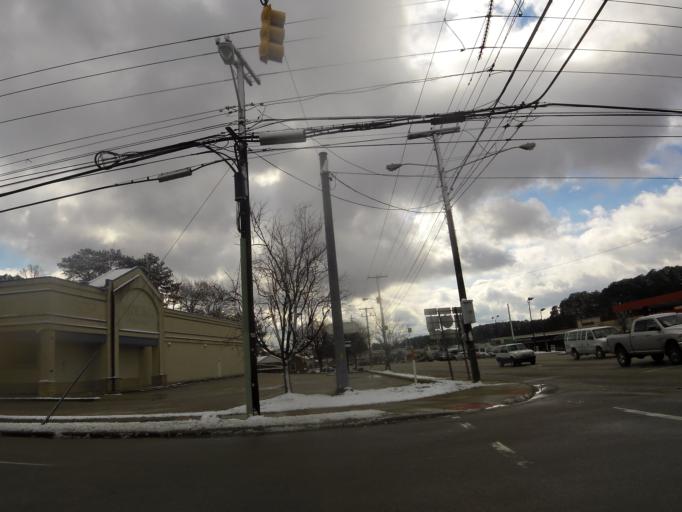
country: US
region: North Carolina
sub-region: Wilson County
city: Wilson
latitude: 35.7219
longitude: -77.9352
